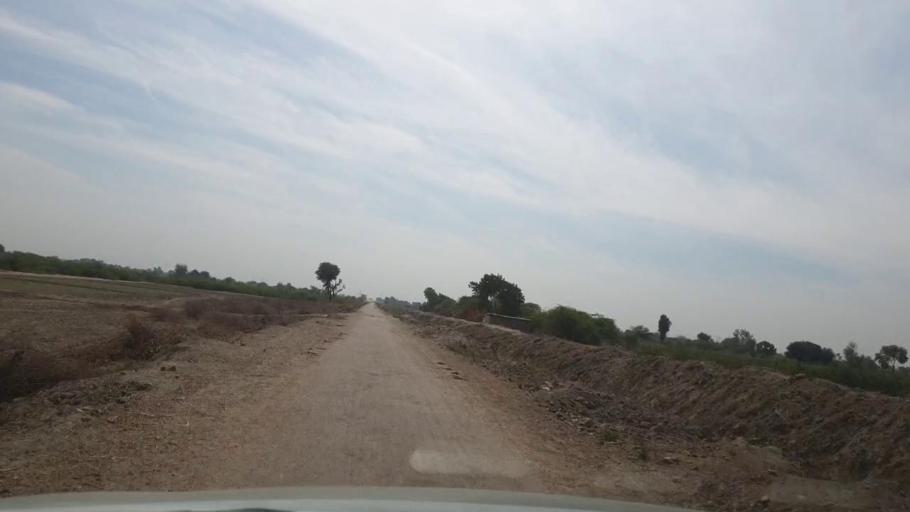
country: PK
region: Sindh
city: Nabisar
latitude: 25.0718
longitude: 69.5789
